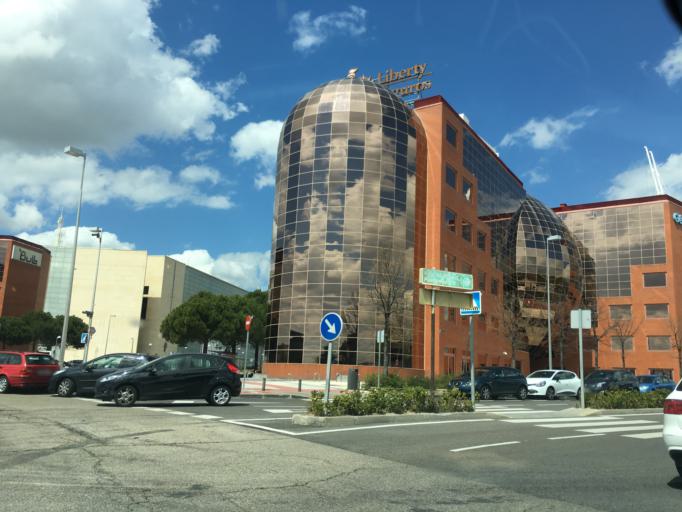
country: ES
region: Madrid
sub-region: Provincia de Madrid
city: San Blas
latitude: 40.4607
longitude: -3.6150
